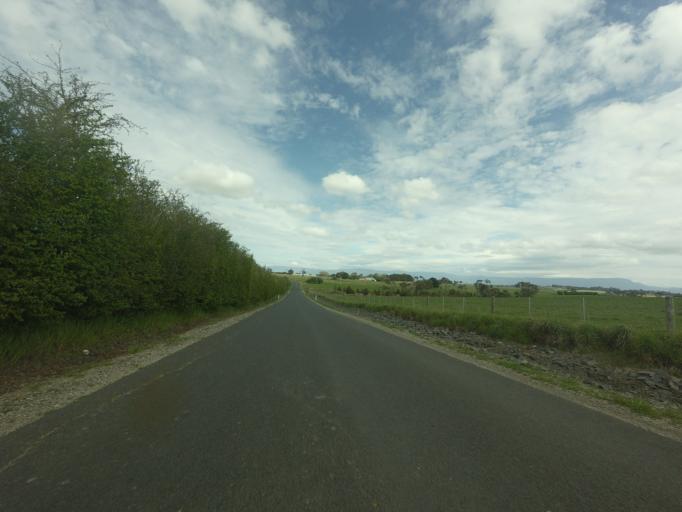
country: AU
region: Tasmania
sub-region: Northern Midlands
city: Longford
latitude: -41.6290
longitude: 147.1560
